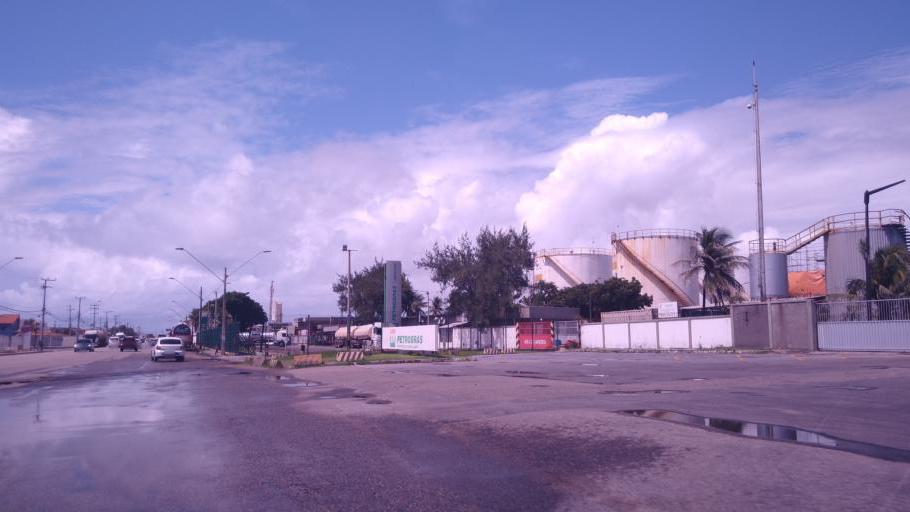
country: BR
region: Ceara
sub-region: Fortaleza
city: Fortaleza
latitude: -3.7161
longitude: -38.4691
